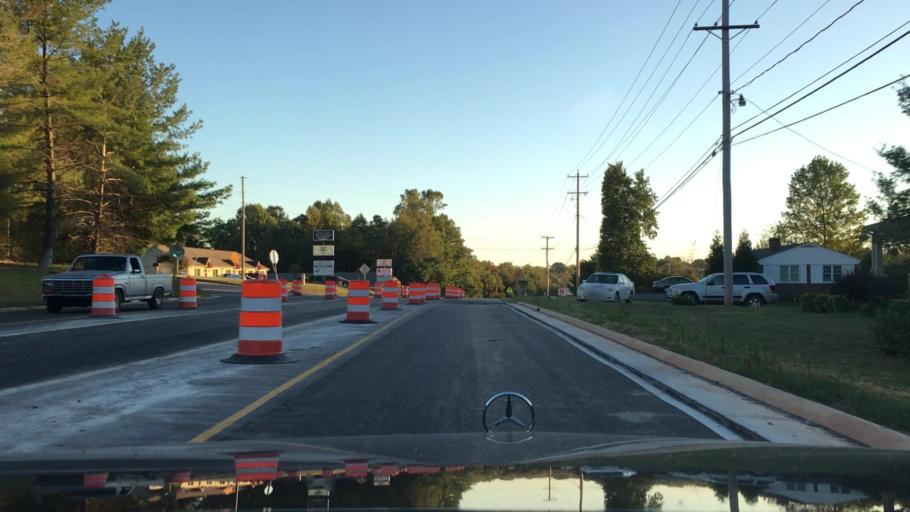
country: US
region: Virginia
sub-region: Campbell County
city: Timberlake
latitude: 37.3323
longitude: -79.2157
